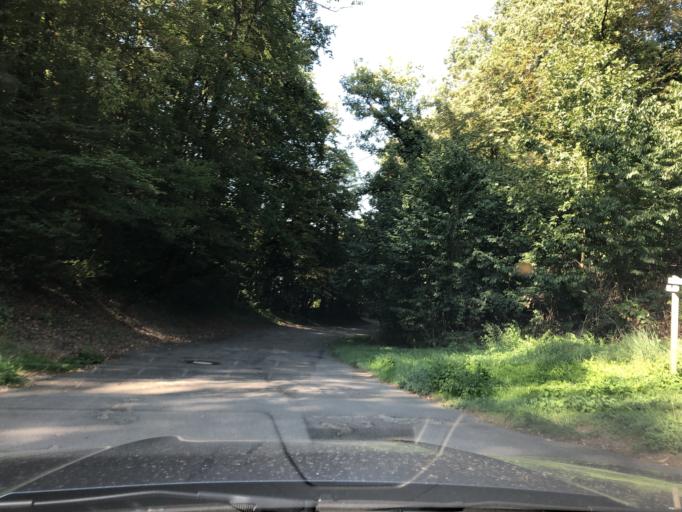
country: DE
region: Baden-Wuerttemberg
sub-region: Karlsruhe Region
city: Leimen
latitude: 49.3651
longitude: 8.7016
